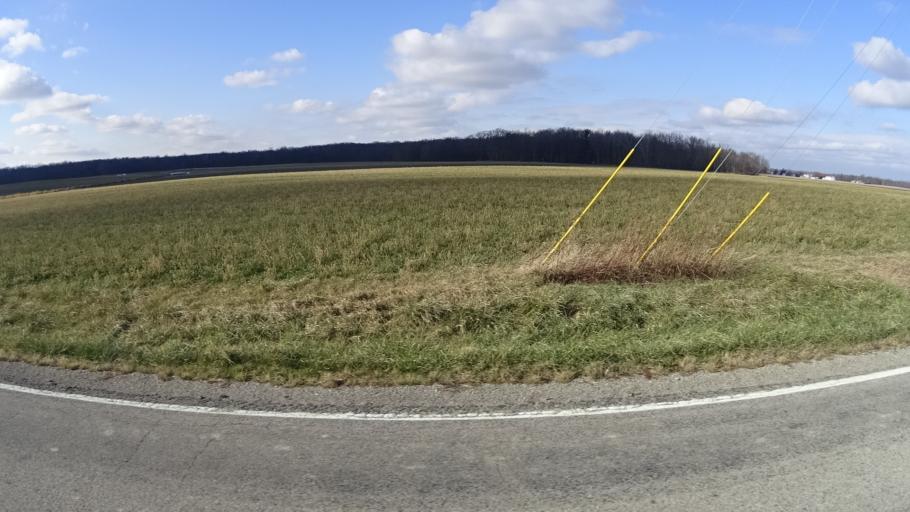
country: US
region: Ohio
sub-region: Lorain County
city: Camden
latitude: 41.2314
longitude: -82.2562
